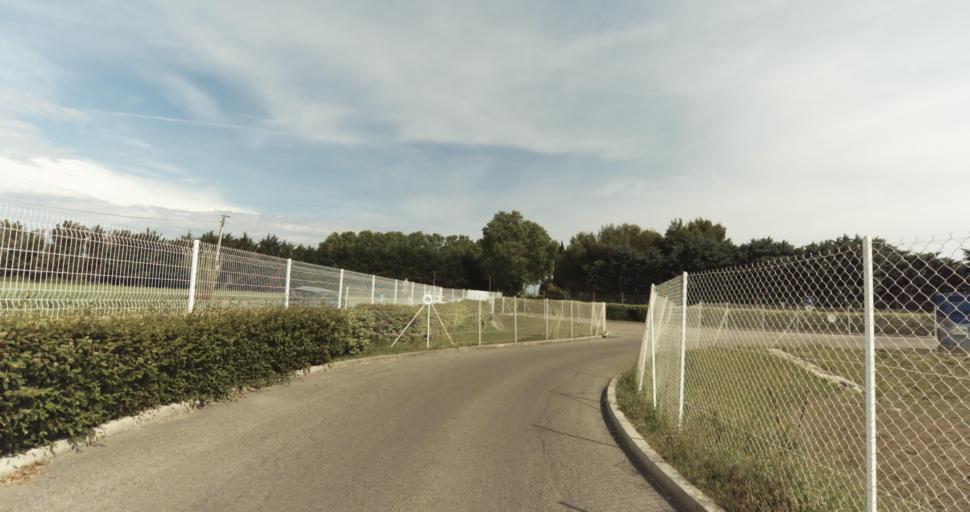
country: FR
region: Languedoc-Roussillon
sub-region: Departement du Gard
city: Caissargues
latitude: 43.8158
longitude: 4.3704
